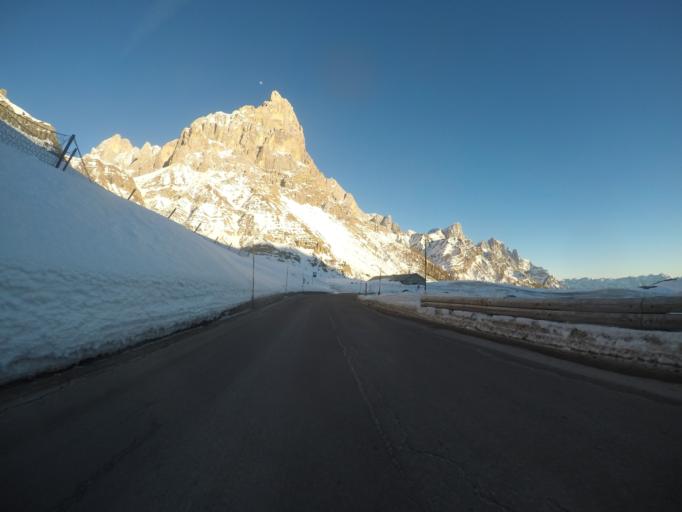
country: IT
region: Veneto
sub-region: Provincia di Belluno
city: Falcade Alto
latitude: 46.2899
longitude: 11.7979
